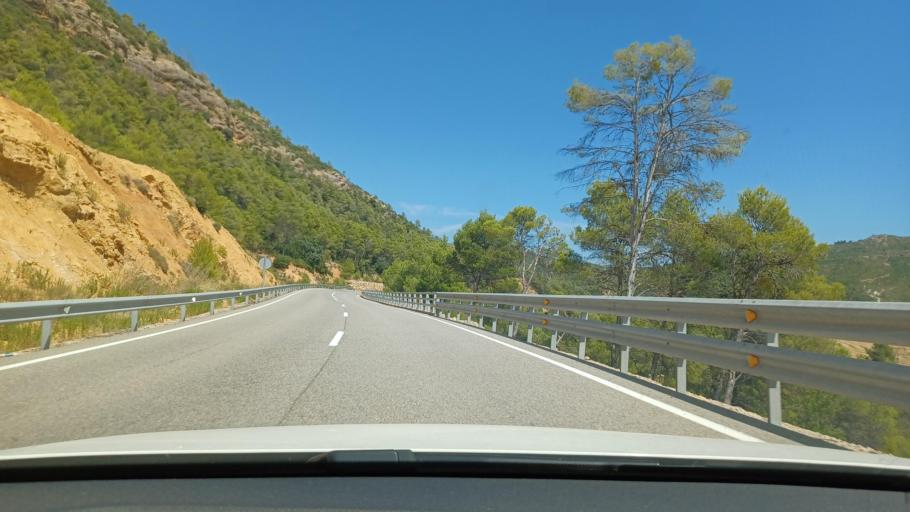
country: ES
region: Catalonia
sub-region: Provincia de Tarragona
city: Horta de Sant Joan
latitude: 40.9548
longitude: 0.3479
